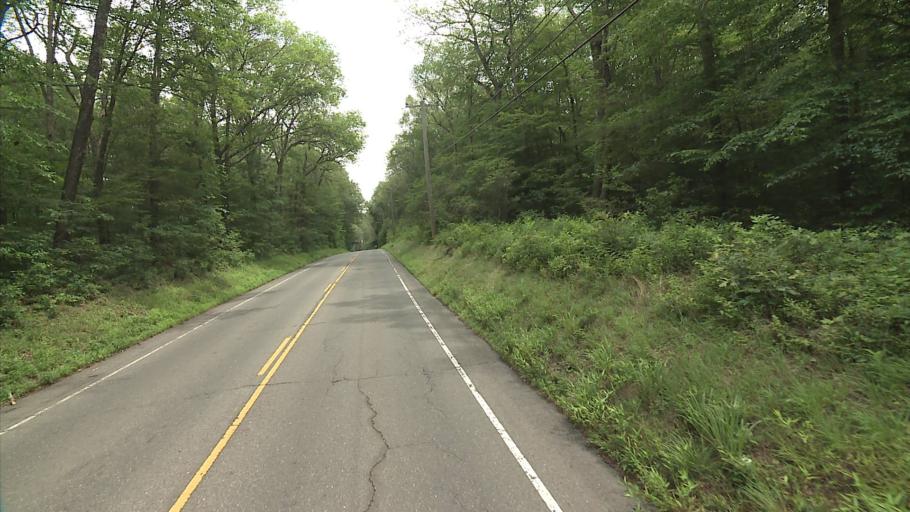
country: US
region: Connecticut
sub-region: Middlesex County
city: Chester Center
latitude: 41.3583
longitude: -72.5147
